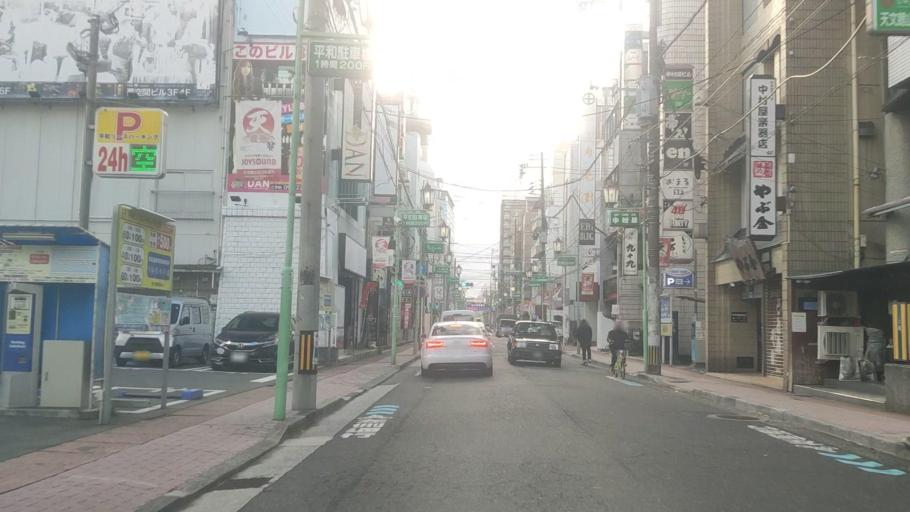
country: JP
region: Kagoshima
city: Kagoshima-shi
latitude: 31.5880
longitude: 130.5542
